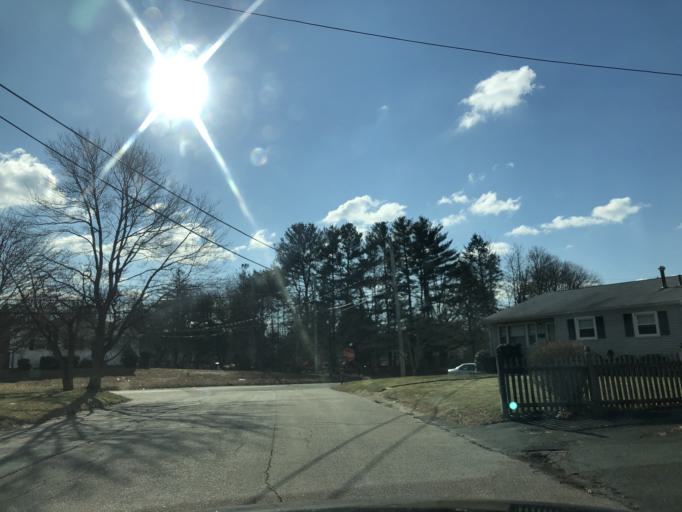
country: US
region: Massachusetts
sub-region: Plymouth County
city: Brockton
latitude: 42.1087
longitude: -71.0053
